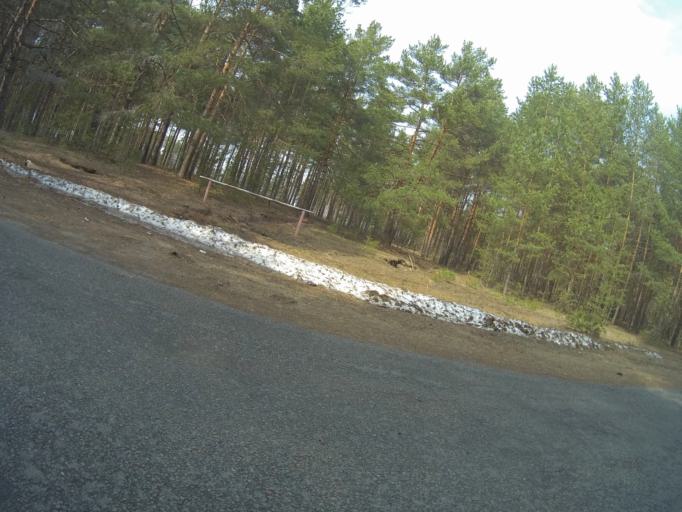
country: RU
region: Vladimir
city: Raduzhnyy
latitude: 56.0354
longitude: 40.3643
